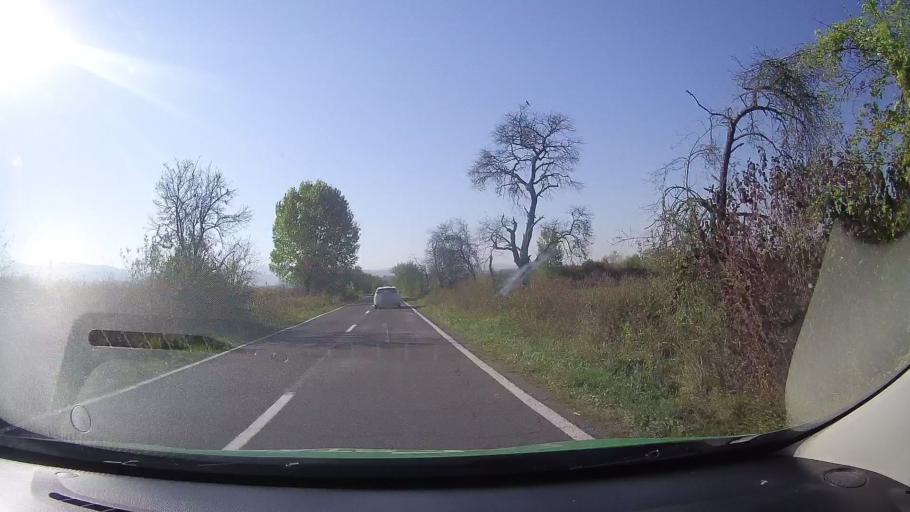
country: RO
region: Timis
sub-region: Comuna Curtea
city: Curtea
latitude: 45.8425
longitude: 22.3117
